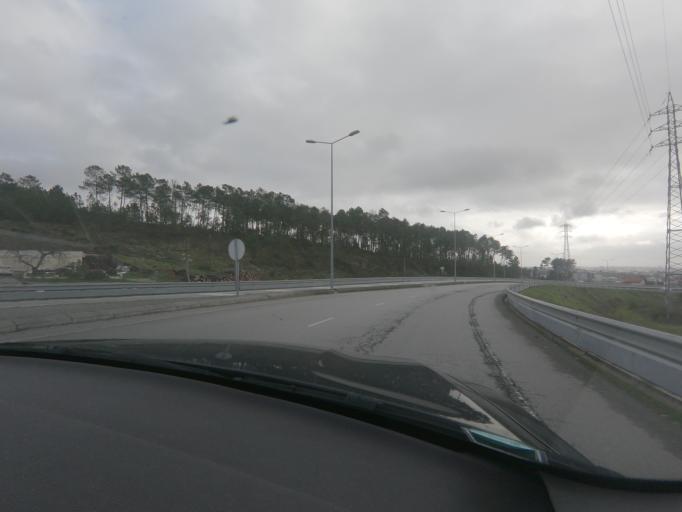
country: PT
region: Viseu
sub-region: Viseu
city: Abraveses
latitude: 40.6984
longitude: -7.9314
